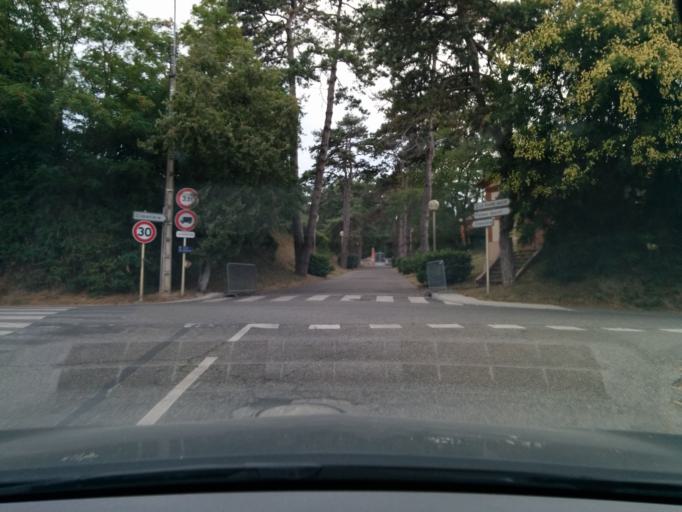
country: FR
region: Midi-Pyrenees
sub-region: Departement de la Haute-Garonne
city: Castanet-Tolosan
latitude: 43.5173
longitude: 1.4960
